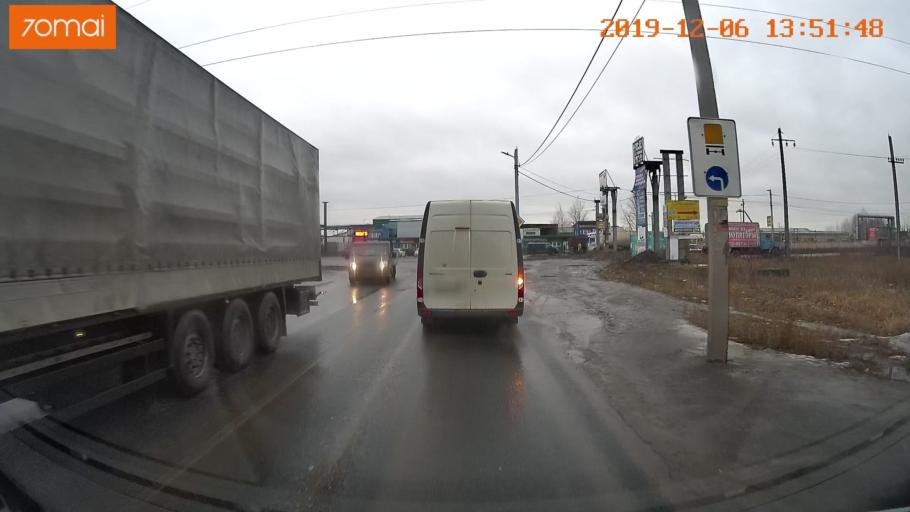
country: RU
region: Ivanovo
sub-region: Gorod Ivanovo
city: Ivanovo
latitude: 56.9663
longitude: 40.9518
